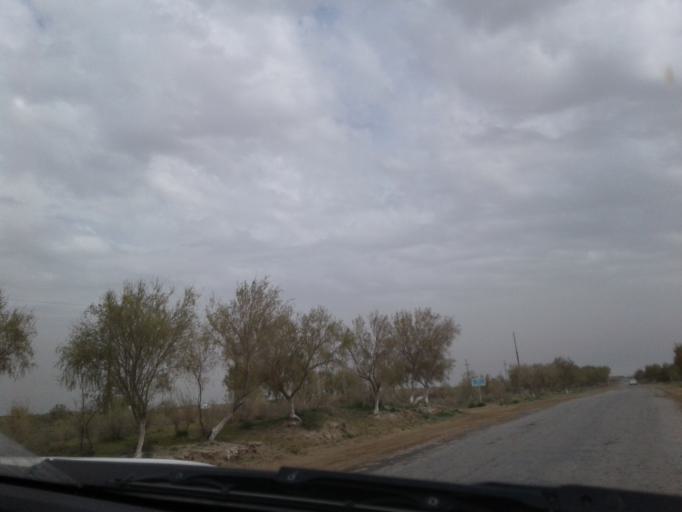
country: TM
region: Lebap
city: Atamyrat
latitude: 38.1709
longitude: 64.9042
